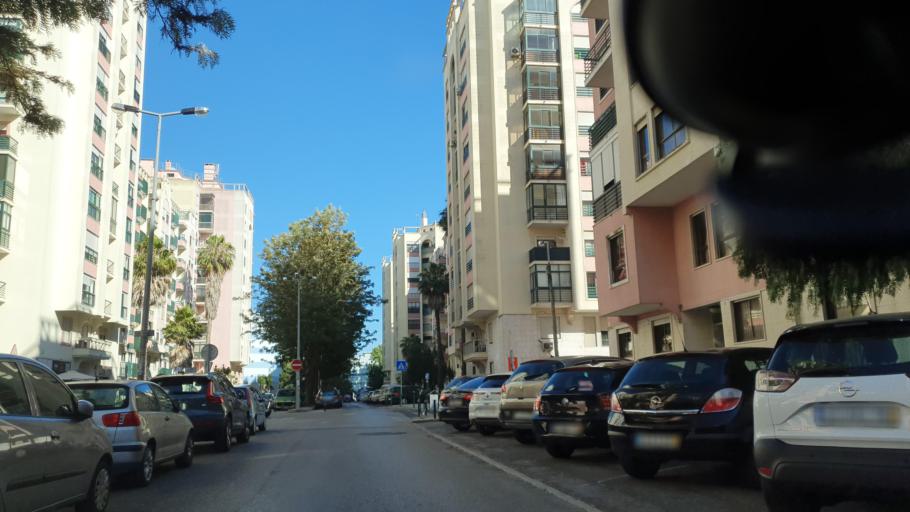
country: PT
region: Lisbon
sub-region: Oeiras
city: Barcarena
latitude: 38.7532
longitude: -9.2789
